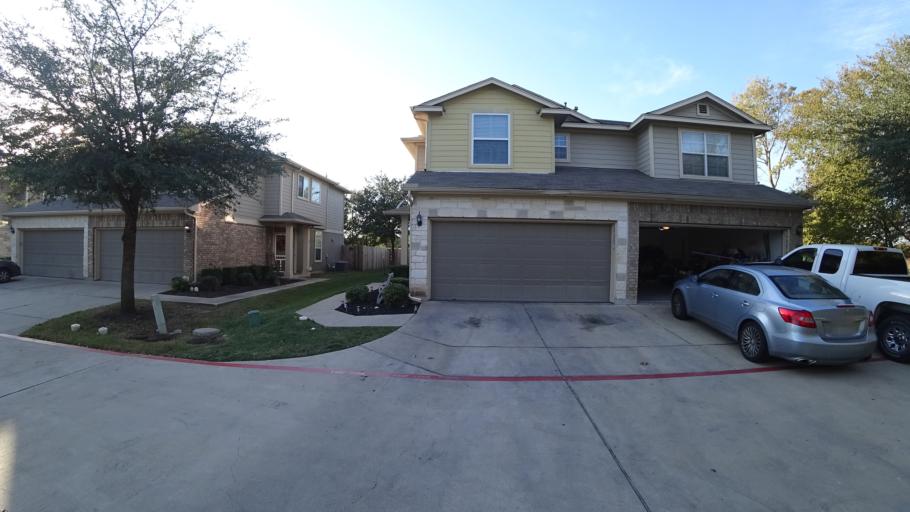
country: US
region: Texas
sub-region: Travis County
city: Pflugerville
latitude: 30.4239
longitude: -97.6446
